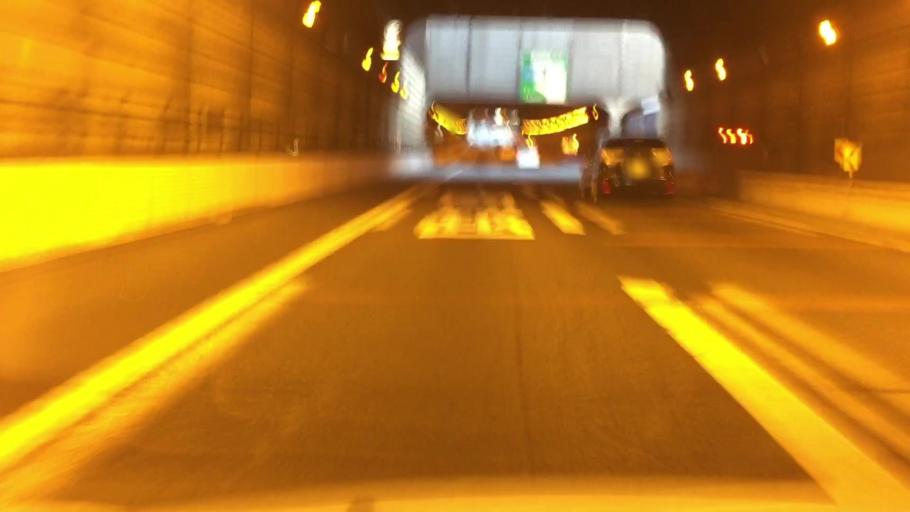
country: JP
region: Saitama
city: Wako
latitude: 35.7672
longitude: 139.6007
